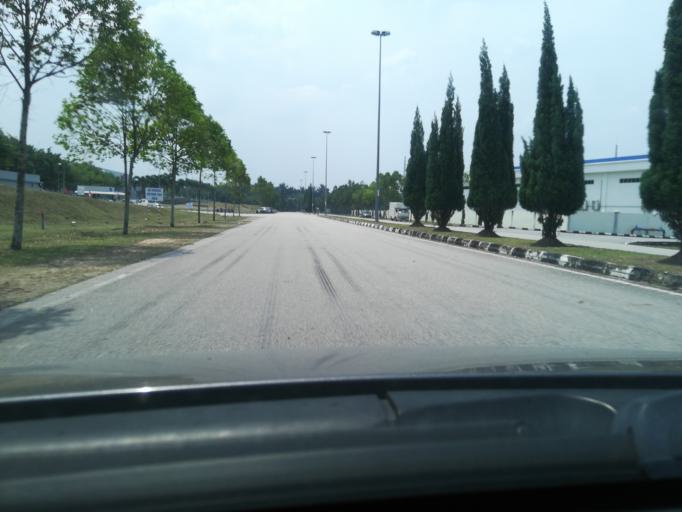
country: MY
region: Kedah
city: Kulim
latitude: 5.4284
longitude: 100.5776
